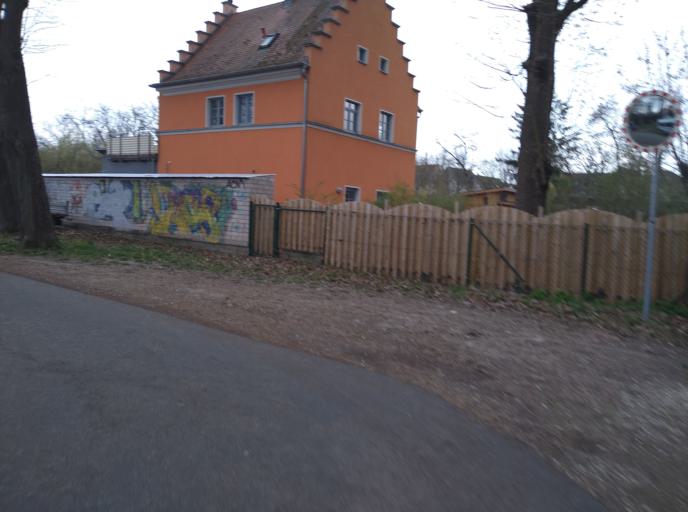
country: DE
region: Bavaria
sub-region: Regierungsbezirk Mittelfranken
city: Nuernberg
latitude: 49.4481
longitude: 11.1114
